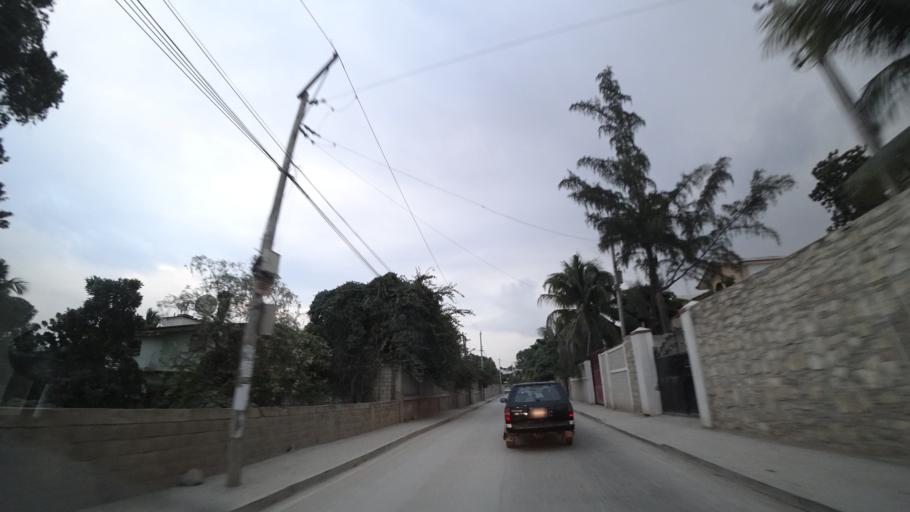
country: HT
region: Ouest
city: Delmas 73
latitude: 18.5523
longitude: -72.2868
